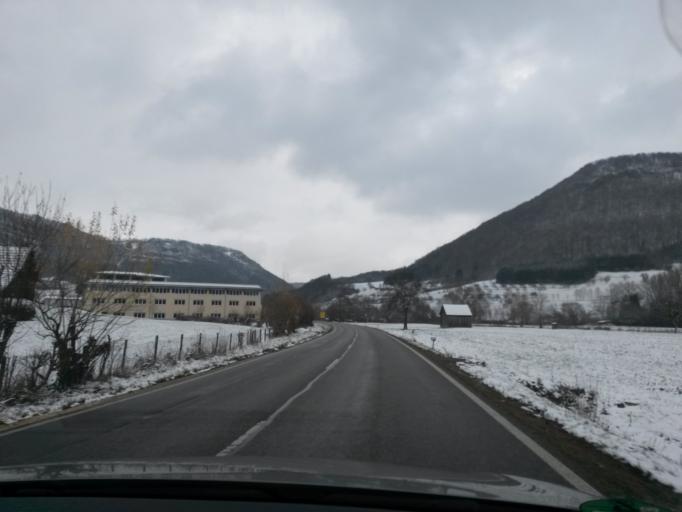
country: DE
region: Baden-Wuerttemberg
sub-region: Regierungsbezirk Stuttgart
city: Deggingen
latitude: 48.6049
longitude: 9.7538
